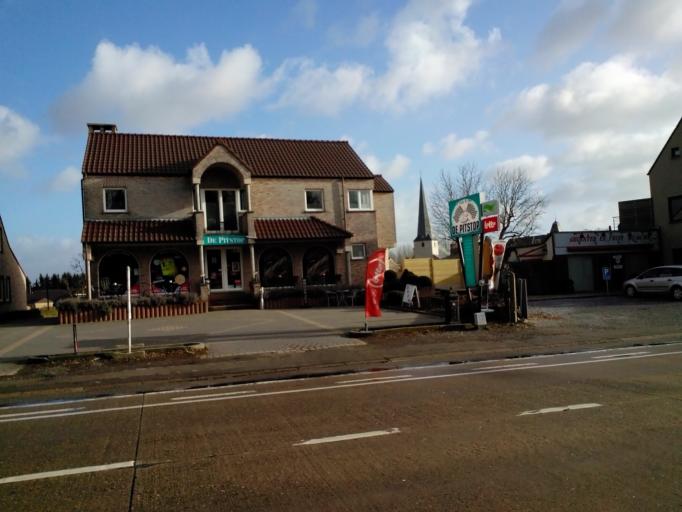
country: BE
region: Flanders
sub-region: Provincie Vlaams-Brabant
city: Boutersem
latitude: 50.8324
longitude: 4.8601
